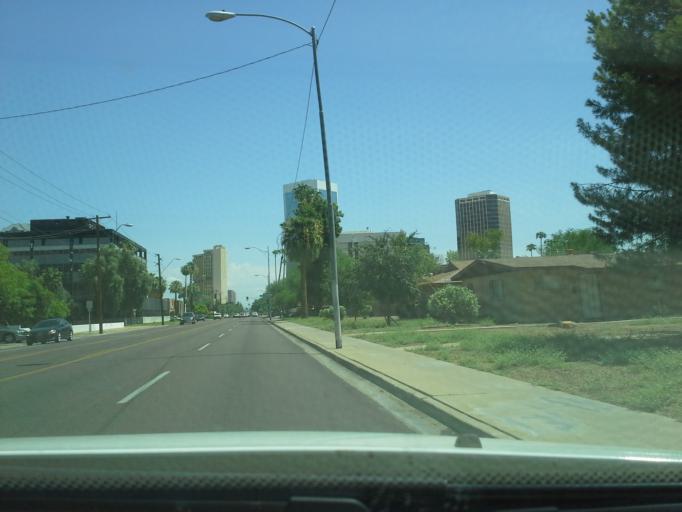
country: US
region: Arizona
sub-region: Maricopa County
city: Phoenix
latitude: 33.4875
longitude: -112.0805
